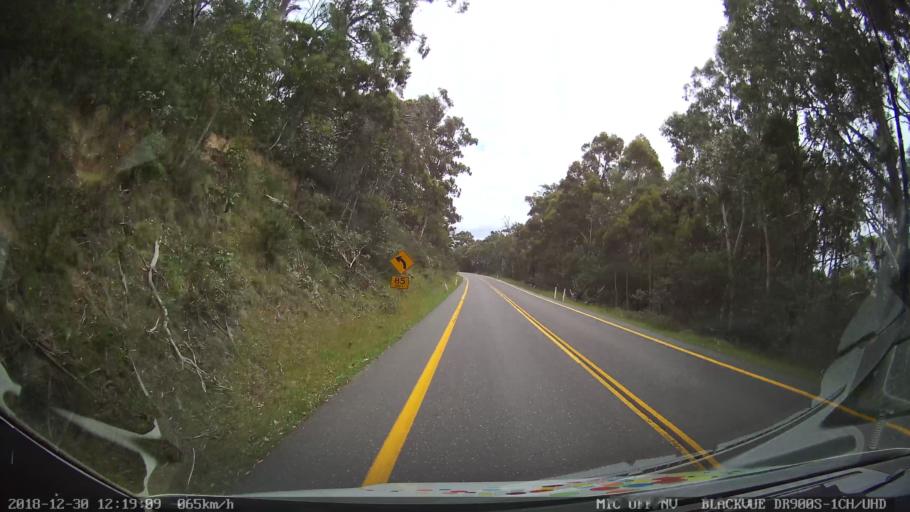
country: AU
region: New South Wales
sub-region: Snowy River
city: Jindabyne
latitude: -36.3471
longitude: 148.5443
